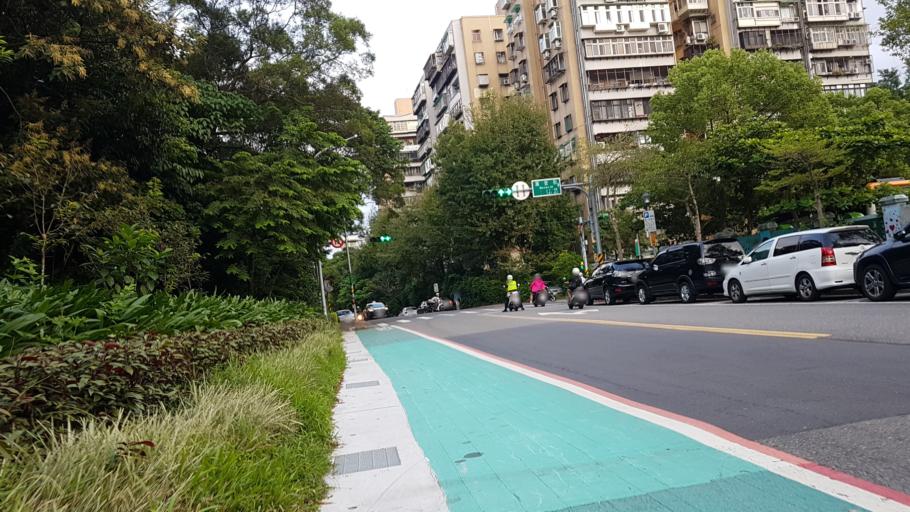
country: TW
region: Taipei
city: Taipei
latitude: 25.0024
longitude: 121.5701
